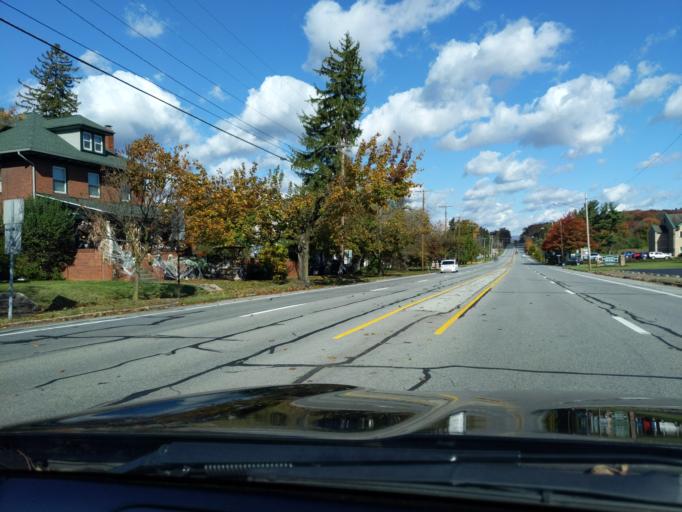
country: US
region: Pennsylvania
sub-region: Blair County
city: Hollidaysburg
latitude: 40.4361
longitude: -78.3921
